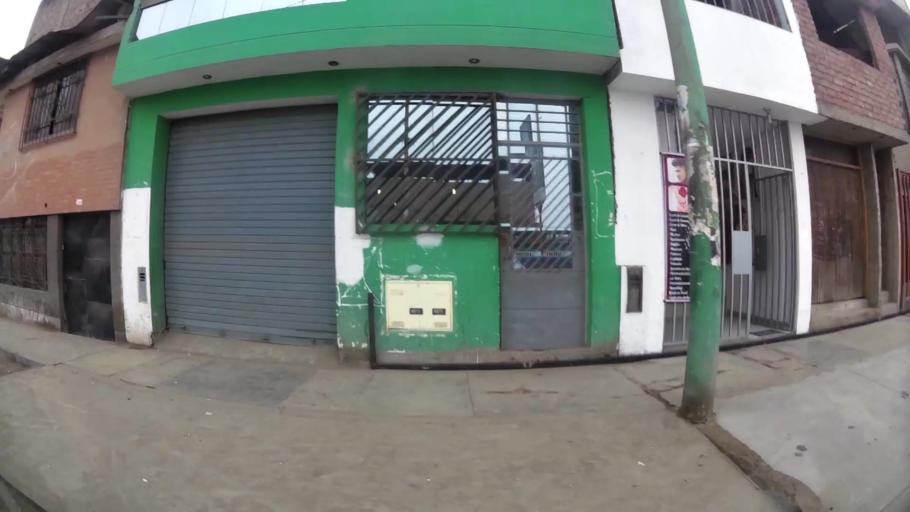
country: PE
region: Lima
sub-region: Lima
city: Surco
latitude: -12.1658
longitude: -76.9606
